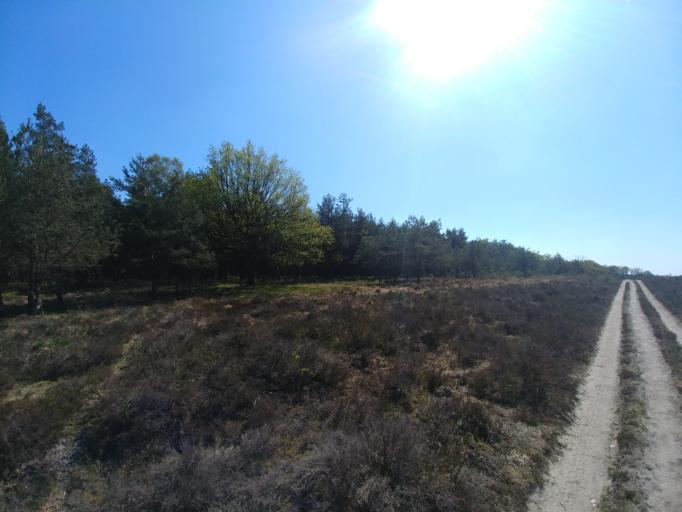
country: NL
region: Gelderland
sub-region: Gemeente Rozendaal
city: Rozendaal
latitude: 52.0659
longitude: 5.9175
